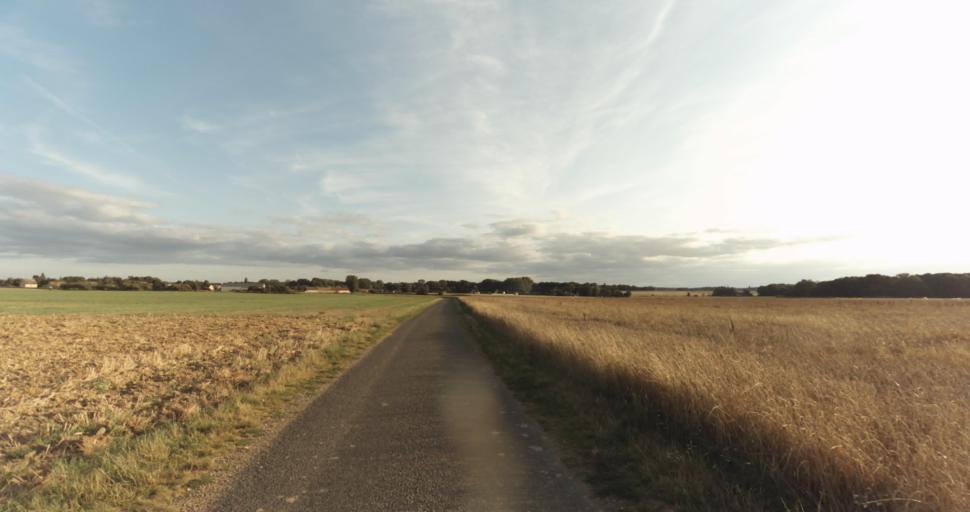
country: FR
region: Haute-Normandie
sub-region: Departement de l'Eure
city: Saint-Germain-sur-Avre
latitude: 48.8278
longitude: 1.2658
